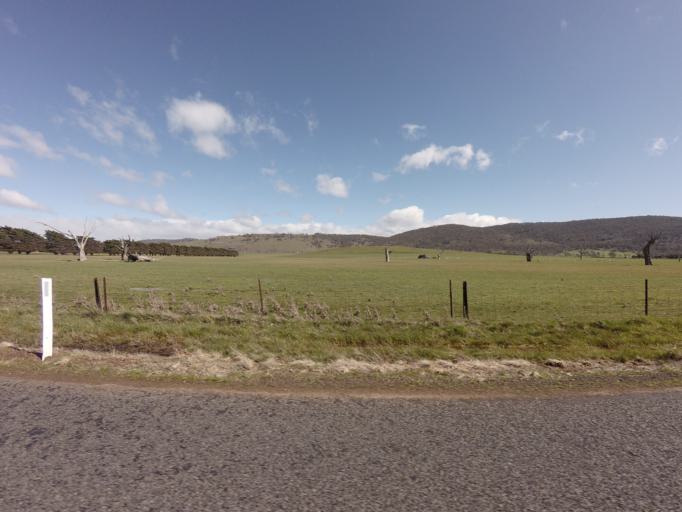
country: AU
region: Tasmania
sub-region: Northern Midlands
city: Evandale
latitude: -41.9923
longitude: 147.4531
